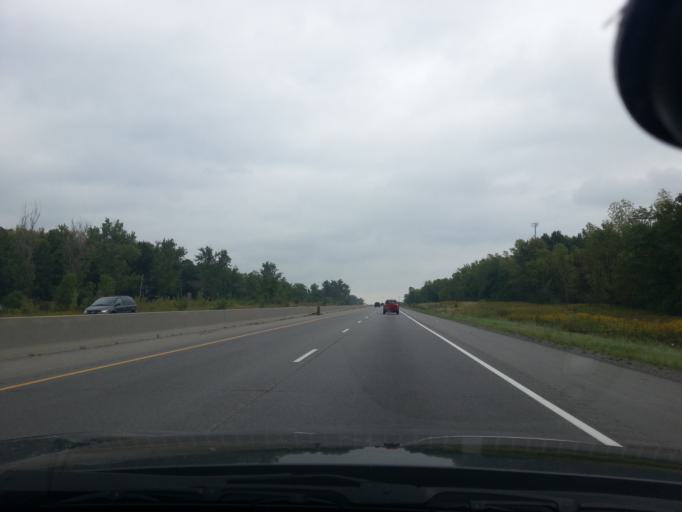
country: CA
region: Ontario
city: Brockville
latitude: 44.6468
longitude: -75.6343
